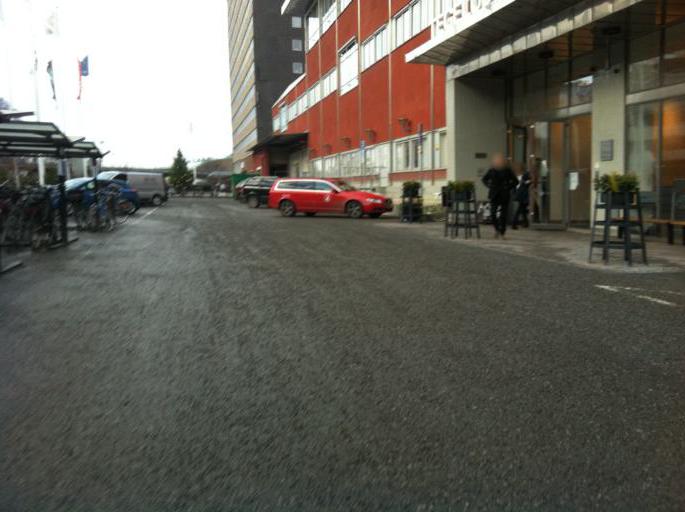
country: SE
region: Stockholm
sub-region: Stockholms Kommun
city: OEstermalm
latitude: 59.3493
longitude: 18.1010
